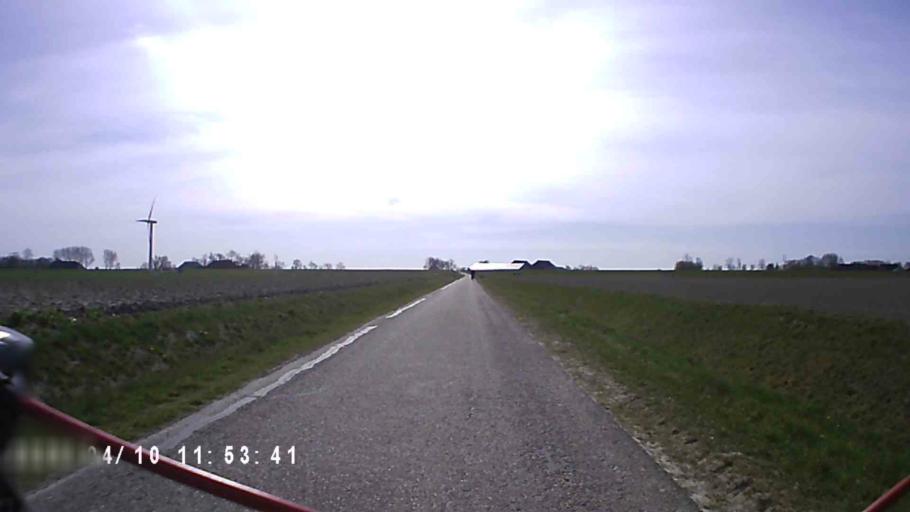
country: NL
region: Groningen
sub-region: Gemeente De Marne
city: Ulrum
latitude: 53.3910
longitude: 6.3318
